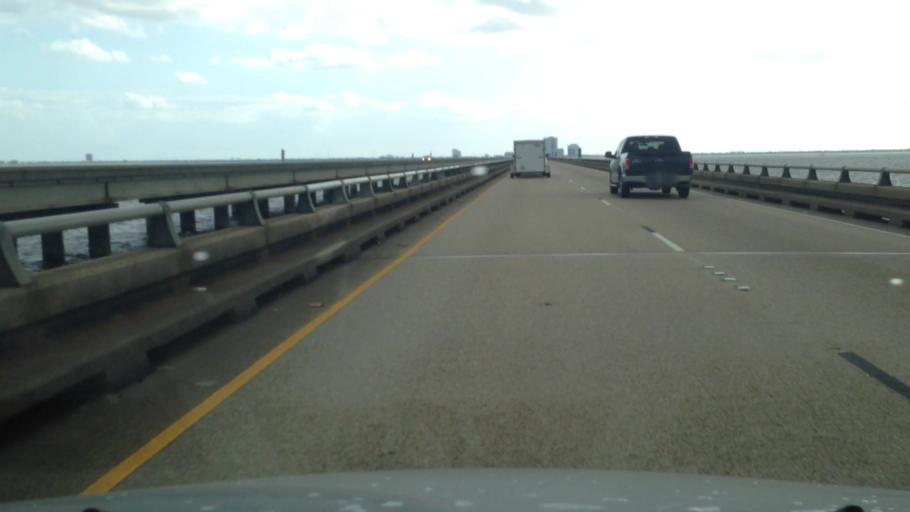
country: US
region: Louisiana
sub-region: Jefferson Parish
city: Metairie
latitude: 30.0676
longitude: -90.1460
